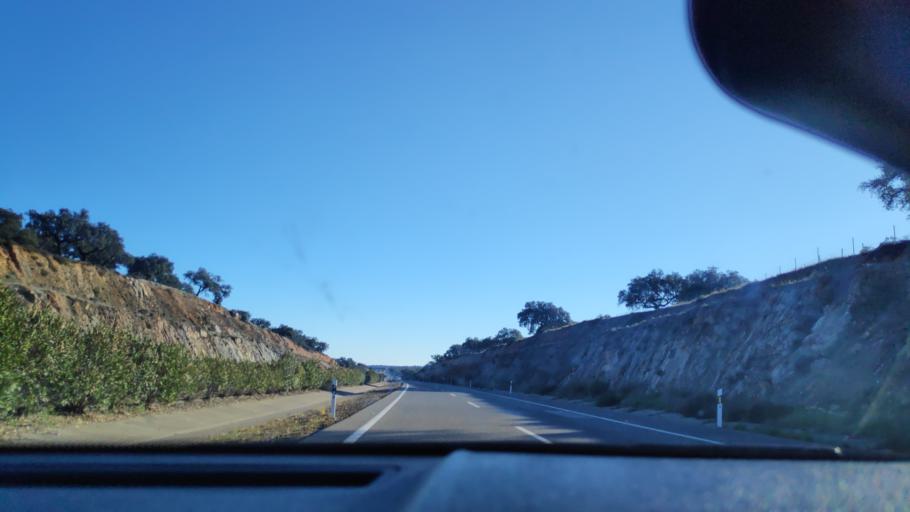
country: ES
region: Andalusia
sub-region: Provincia de Huelva
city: Santa Olalla del Cala
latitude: 37.9663
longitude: -6.2355
